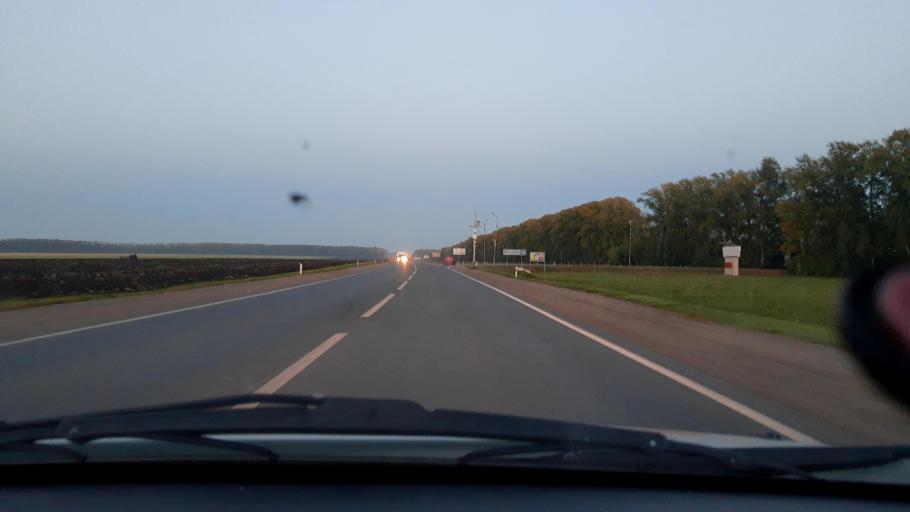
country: RU
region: Bashkortostan
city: Karmaskaly
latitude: 54.3852
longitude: 56.1496
